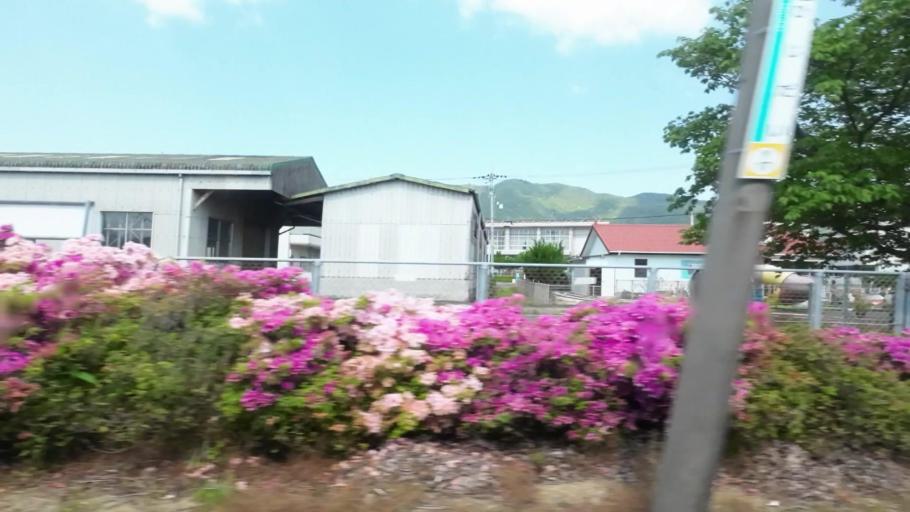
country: JP
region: Kagawa
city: Kan'onjicho
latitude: 34.1671
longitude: 133.6904
